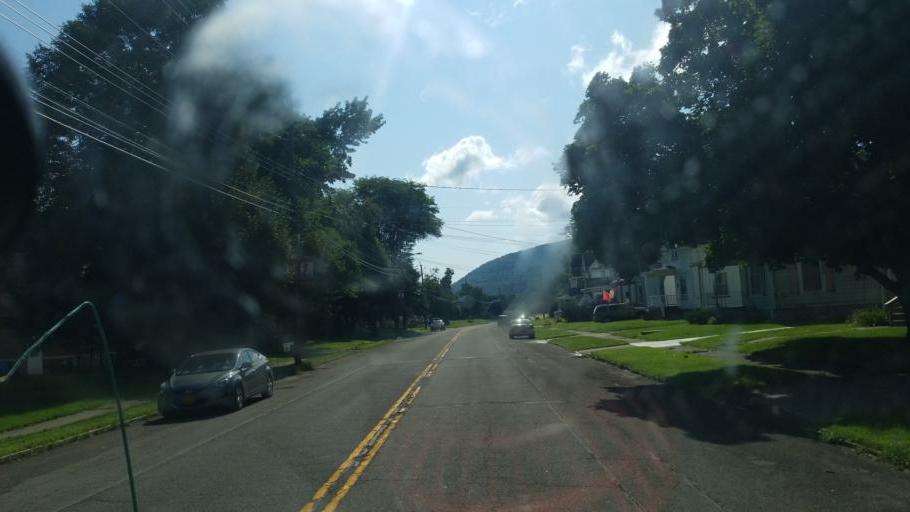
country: US
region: New York
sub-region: Steuben County
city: Canisteo
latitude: 42.2684
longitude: -77.5998
